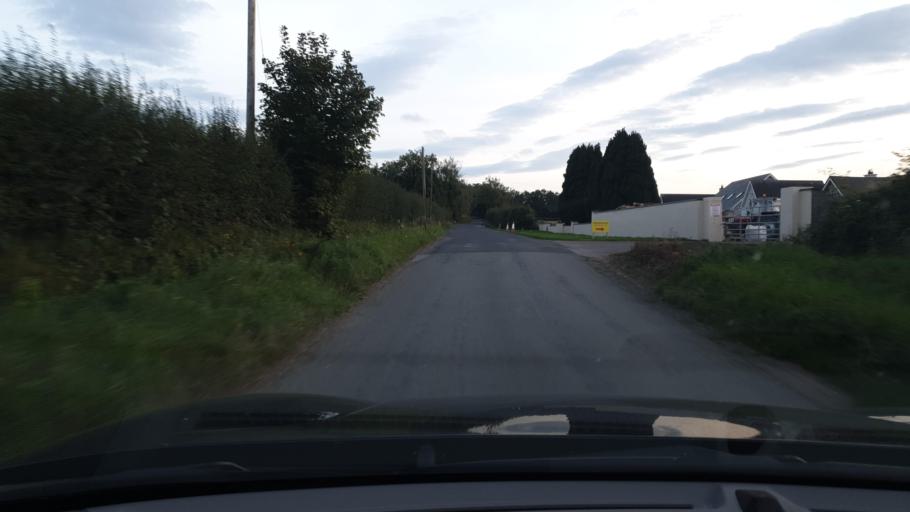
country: IE
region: Leinster
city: Balrothery
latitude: 53.5733
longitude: -6.1990
